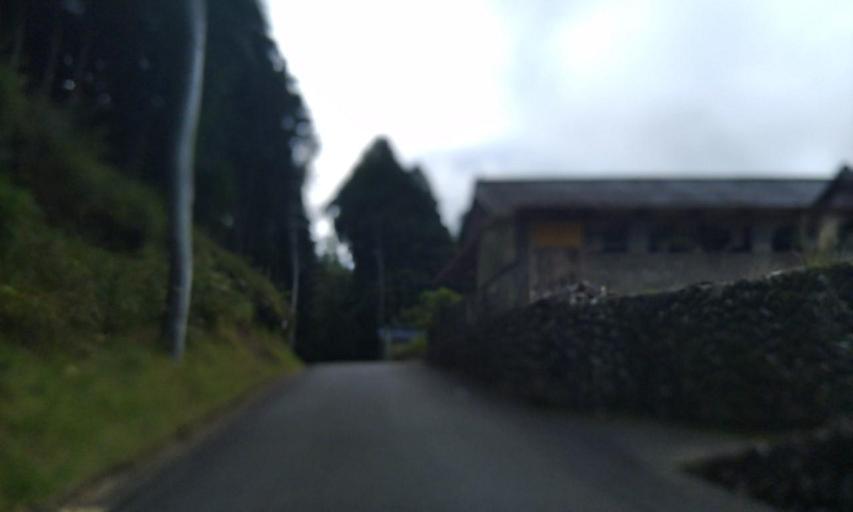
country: JP
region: Wakayama
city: Shingu
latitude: 33.9320
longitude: 135.9796
